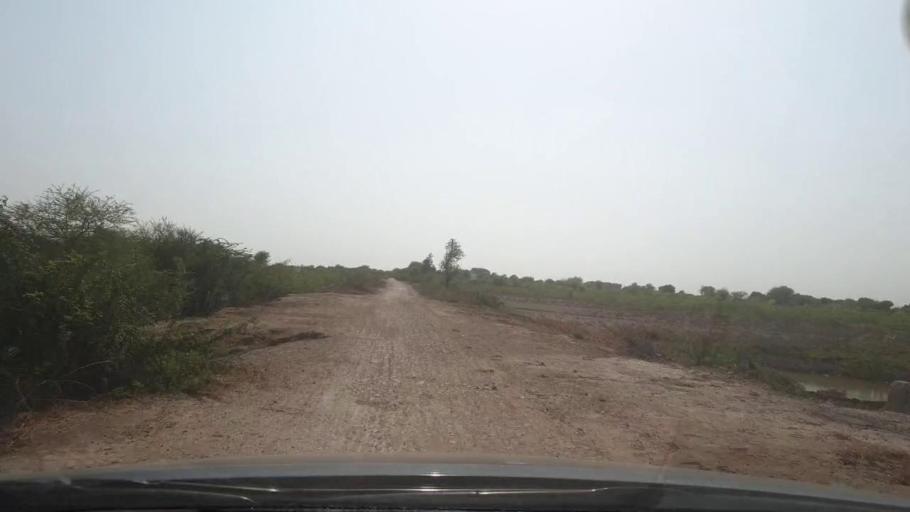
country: PK
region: Sindh
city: Naukot
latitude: 24.7867
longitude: 69.2025
